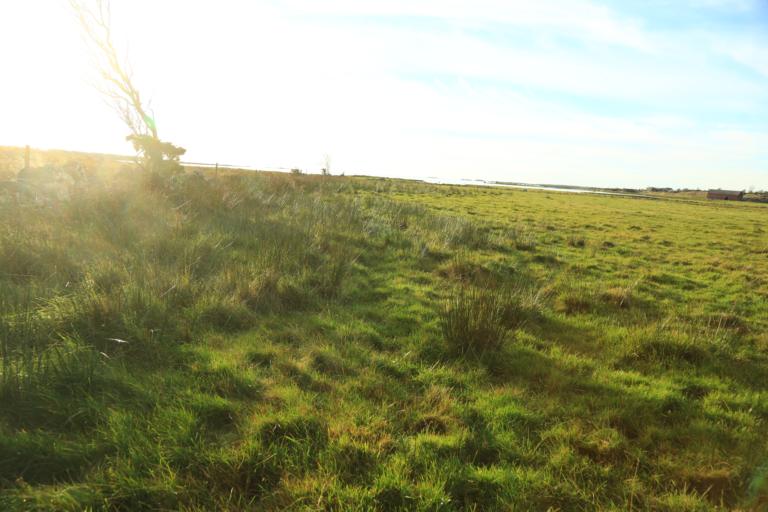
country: SE
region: Halland
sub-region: Varbergs Kommun
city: Varberg
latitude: 57.1626
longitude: 12.2315
